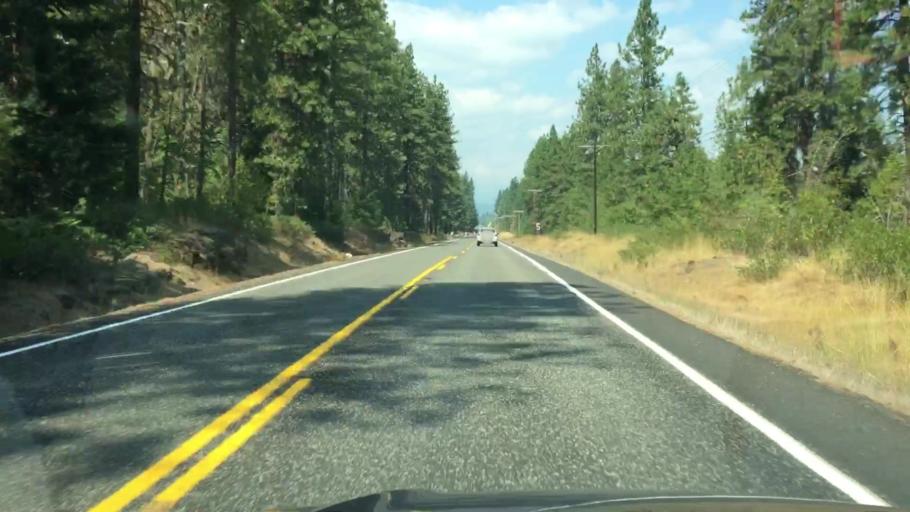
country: US
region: Washington
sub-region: Klickitat County
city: White Salmon
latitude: 45.9810
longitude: -121.5080
